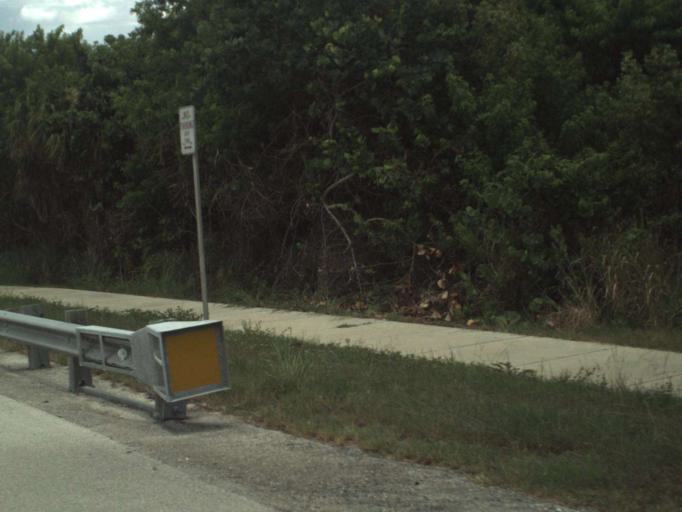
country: US
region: Florida
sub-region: Saint Lucie County
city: Hutchinson Island South
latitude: 27.3538
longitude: -80.2456
